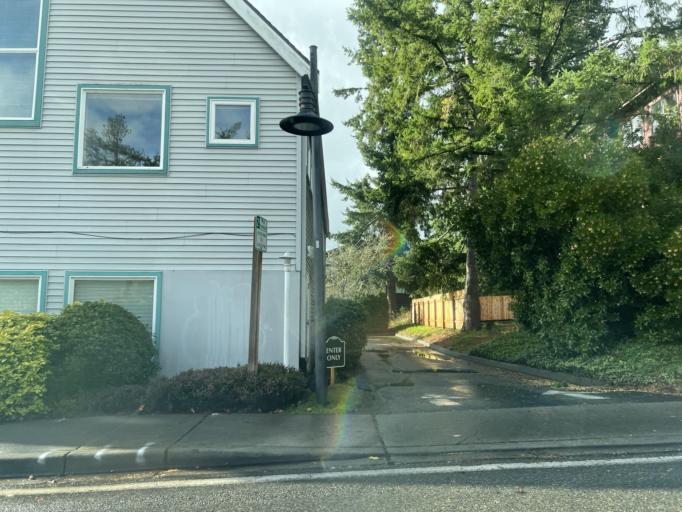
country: US
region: Washington
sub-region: Kitsap County
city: Bainbridge Island
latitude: 47.6275
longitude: -122.5170
